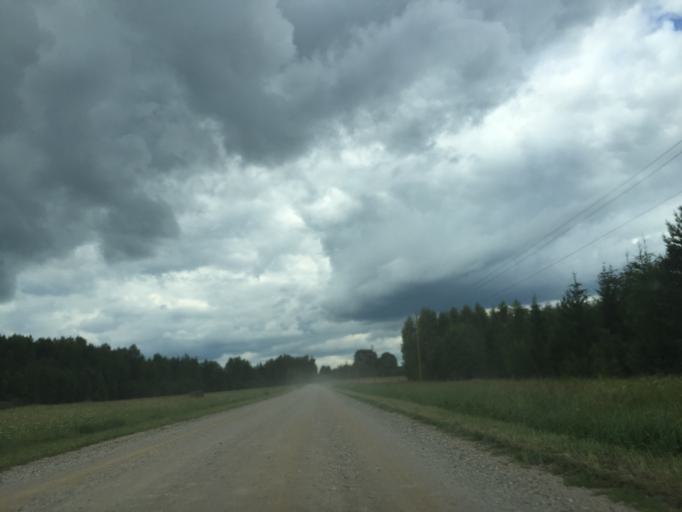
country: LV
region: Malpils
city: Malpils
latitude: 56.8682
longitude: 25.0096
